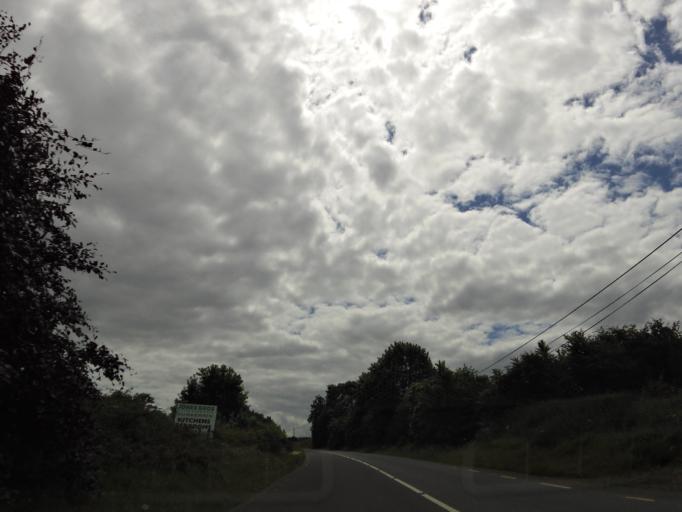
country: IE
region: Munster
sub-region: North Tipperary
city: Templemore
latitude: 52.7705
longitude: -8.0257
